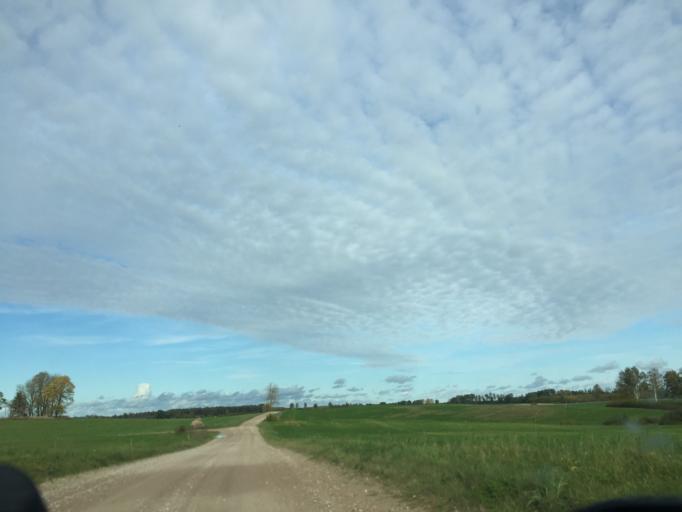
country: LV
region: Jaunpils
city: Jaunpils
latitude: 56.6241
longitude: 23.0618
